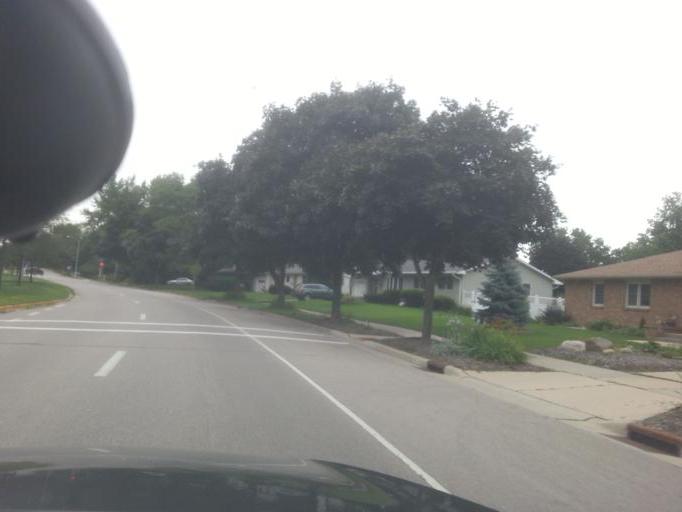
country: US
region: Wisconsin
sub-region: Dane County
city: Shorewood Hills
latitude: 43.0668
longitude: -89.4684
